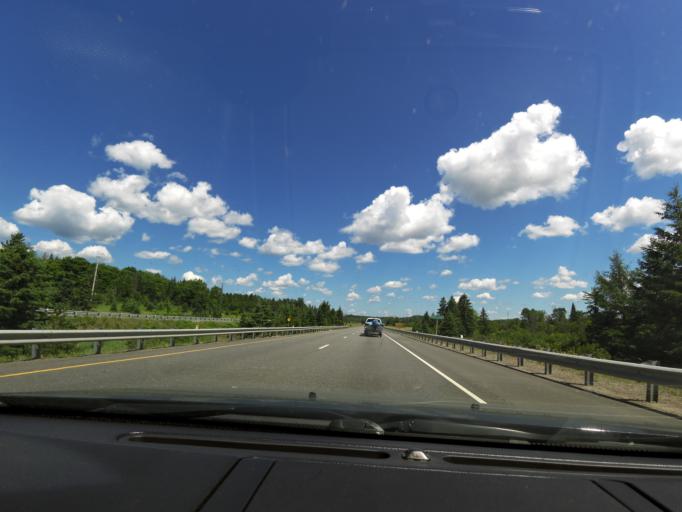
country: CA
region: Ontario
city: Huntsville
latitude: 45.2504
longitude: -79.2973
